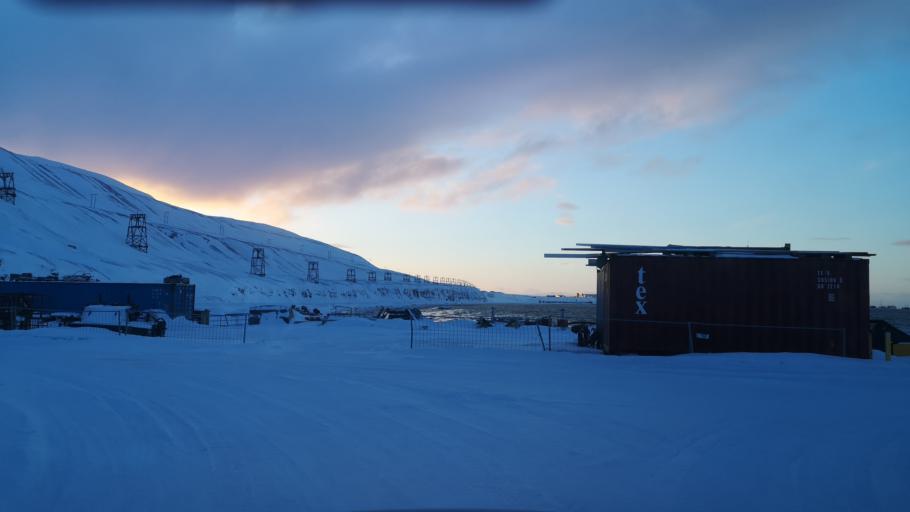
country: SJ
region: Svalbard
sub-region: Spitsbergen
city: Longyearbyen
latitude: 78.2289
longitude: 15.5960
